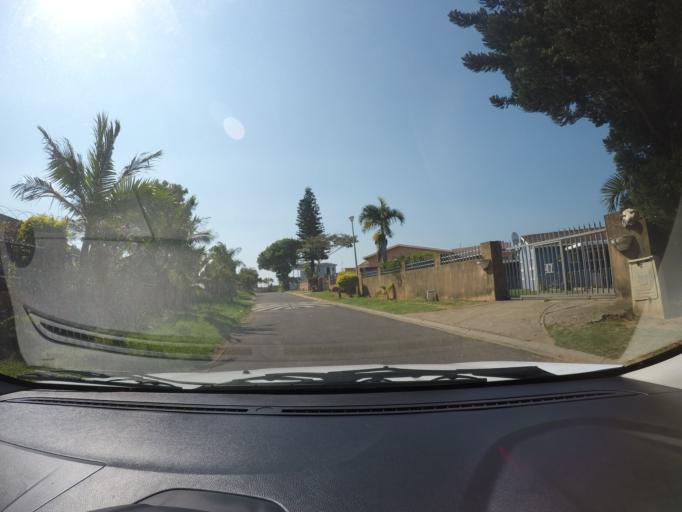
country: ZA
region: KwaZulu-Natal
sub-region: uThungulu District Municipality
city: Richards Bay
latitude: -28.7234
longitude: 32.0469
